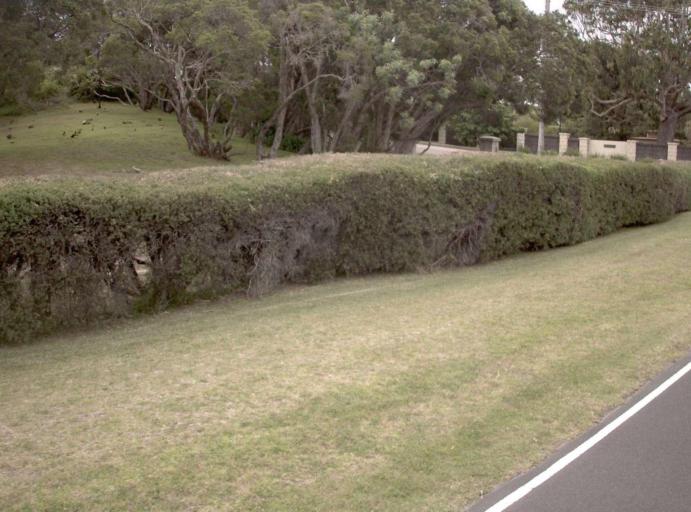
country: AU
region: Victoria
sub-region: Mornington Peninsula
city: Sorrento
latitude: -38.3486
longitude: 144.7610
